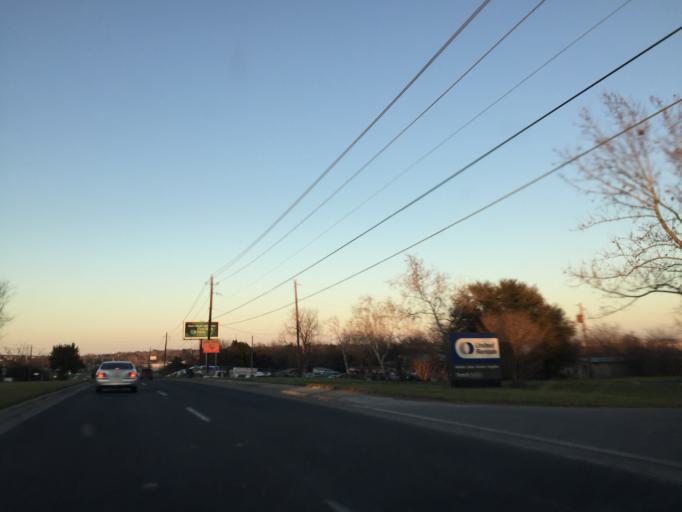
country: US
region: Texas
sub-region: Travis County
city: Pflugerville
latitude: 30.4003
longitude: -97.6405
